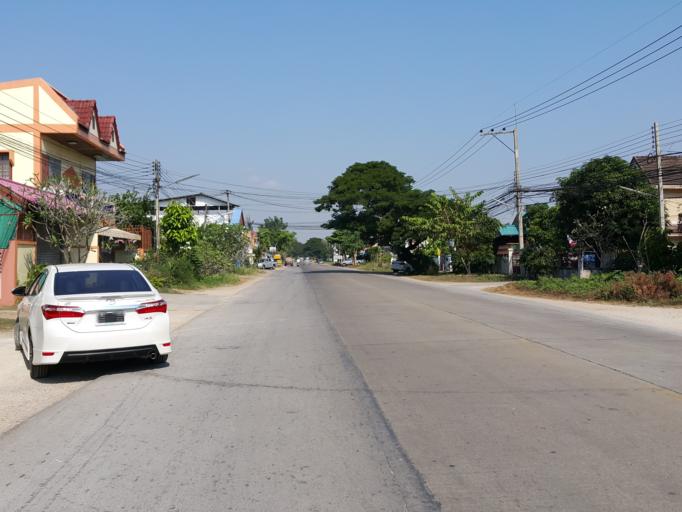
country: TH
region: Lampang
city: Lampang
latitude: 18.3010
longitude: 99.4979
